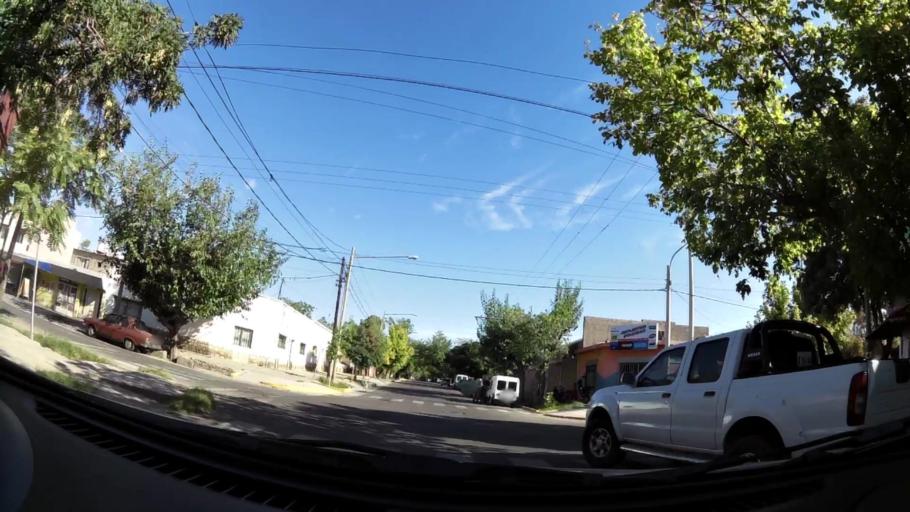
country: AR
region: Mendoza
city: Mendoza
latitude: -32.9050
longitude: -68.8329
